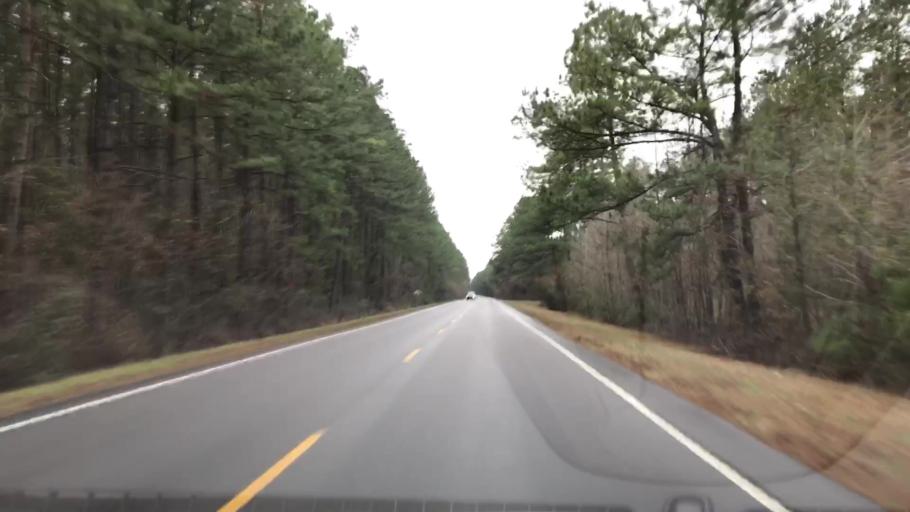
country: US
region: South Carolina
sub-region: Berkeley County
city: Saint Stephen
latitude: 33.2902
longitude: -79.7919
